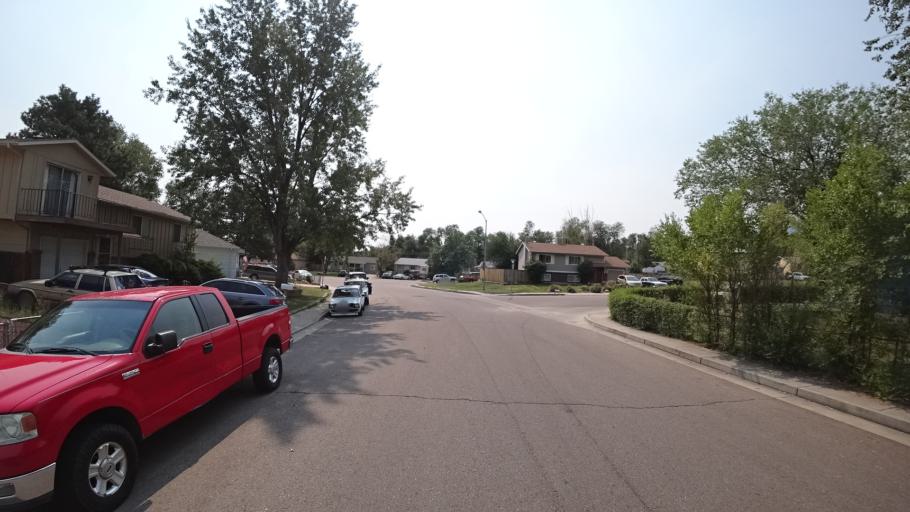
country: US
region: Colorado
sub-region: El Paso County
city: Colorado Springs
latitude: 38.8015
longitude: -104.8136
